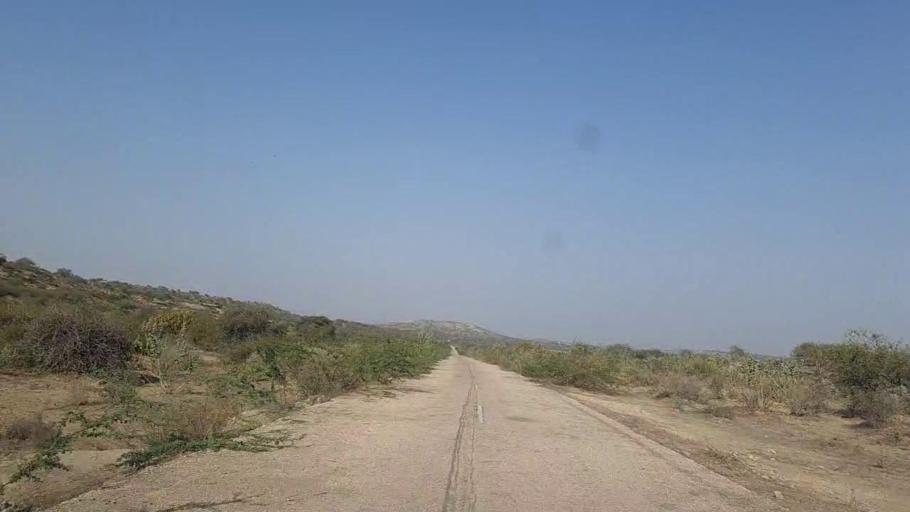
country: PK
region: Sindh
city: Naukot
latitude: 24.6032
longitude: 69.3299
